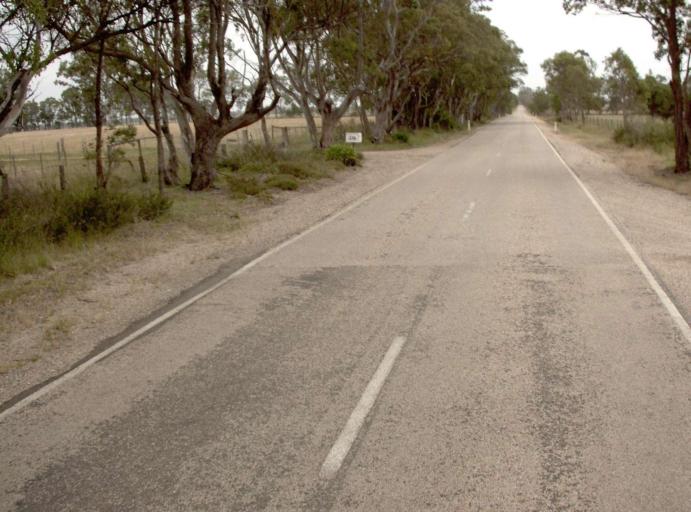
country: AU
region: Victoria
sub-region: East Gippsland
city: Bairnsdale
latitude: -37.8423
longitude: 147.4309
